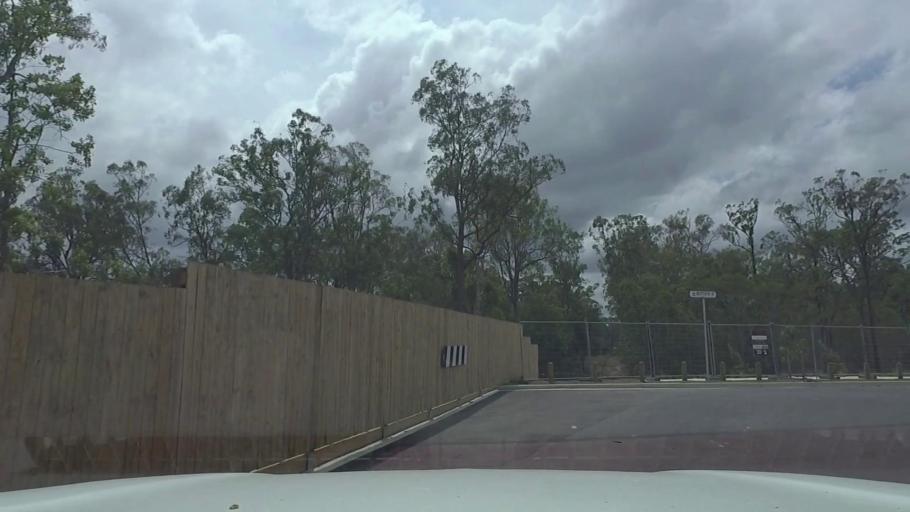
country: AU
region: Queensland
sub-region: Logan
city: Logan Reserve
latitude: -27.7019
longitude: 153.1069
